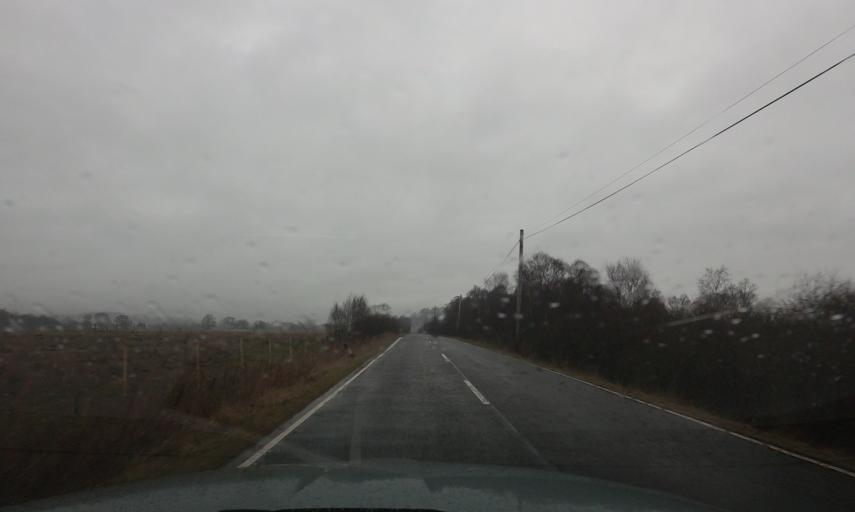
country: GB
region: Scotland
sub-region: Stirling
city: Balfron
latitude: 56.1295
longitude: -4.3586
